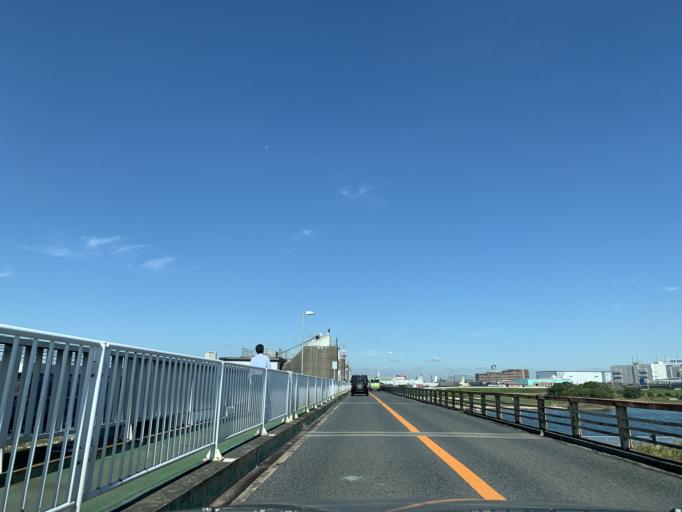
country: JP
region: Tokyo
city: Urayasu
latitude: 35.7021
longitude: 139.9226
